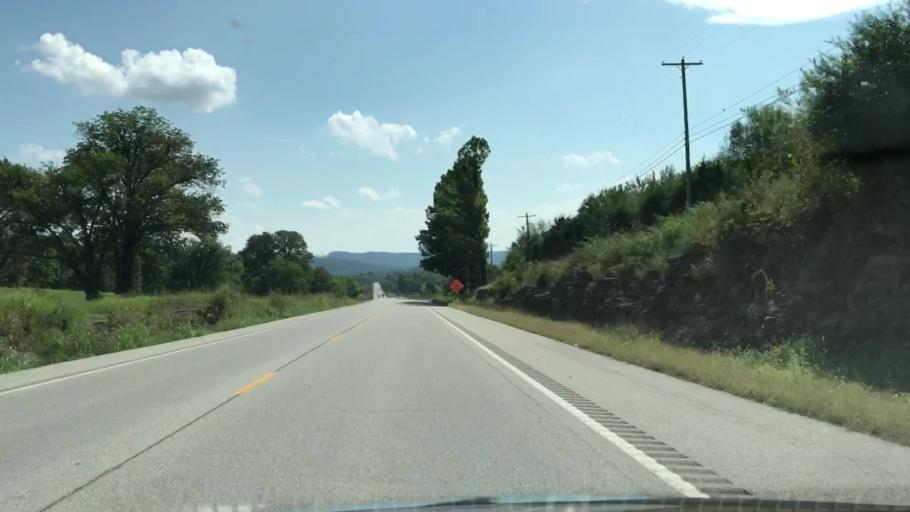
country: US
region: Tennessee
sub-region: Trousdale County
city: Hartsville
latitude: 36.3658
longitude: -86.0795
